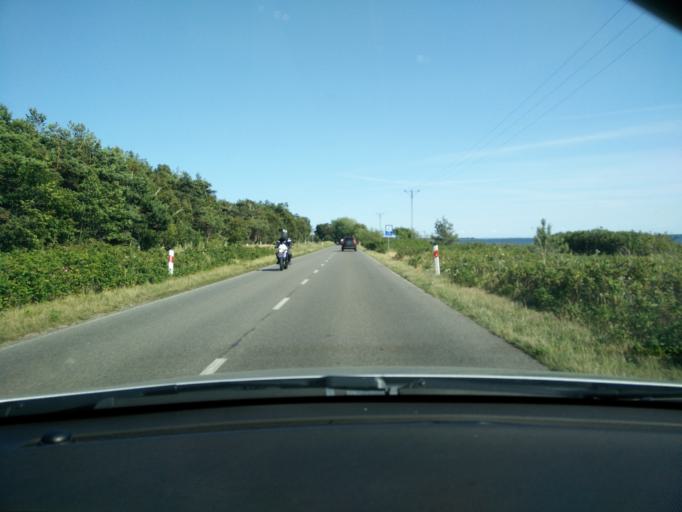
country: PL
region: Pomeranian Voivodeship
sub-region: Powiat pucki
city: Jastarnia
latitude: 54.7264
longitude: 18.6053
